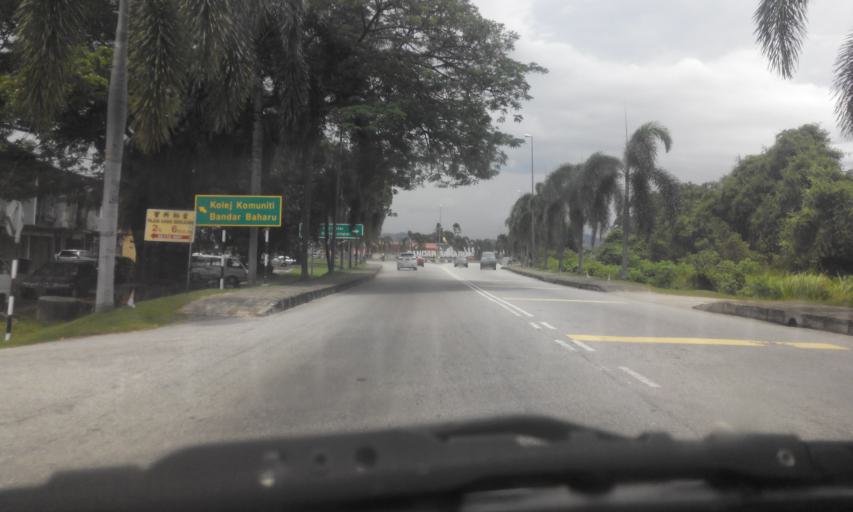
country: MY
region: Perak
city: Parit Buntar
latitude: 5.1302
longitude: 100.4961
